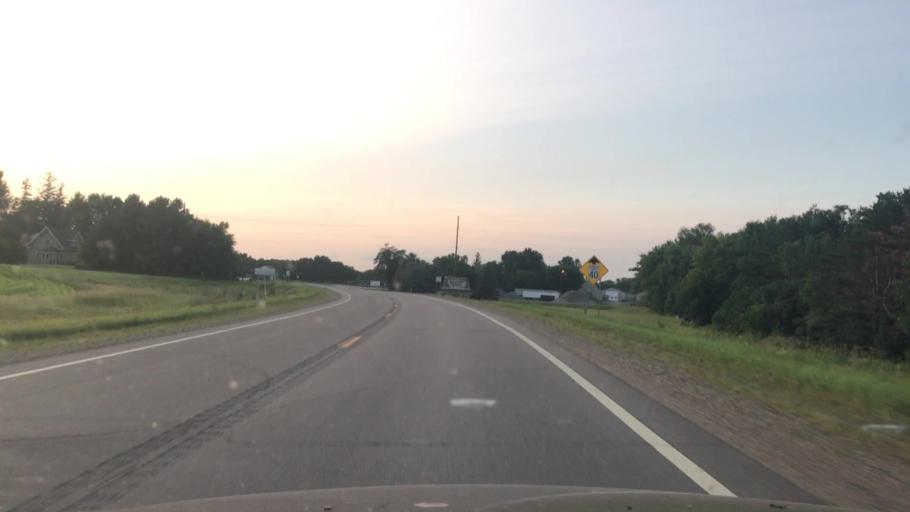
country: US
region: Minnesota
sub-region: Redwood County
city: Redwood Falls
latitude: 44.5234
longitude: -95.1181
